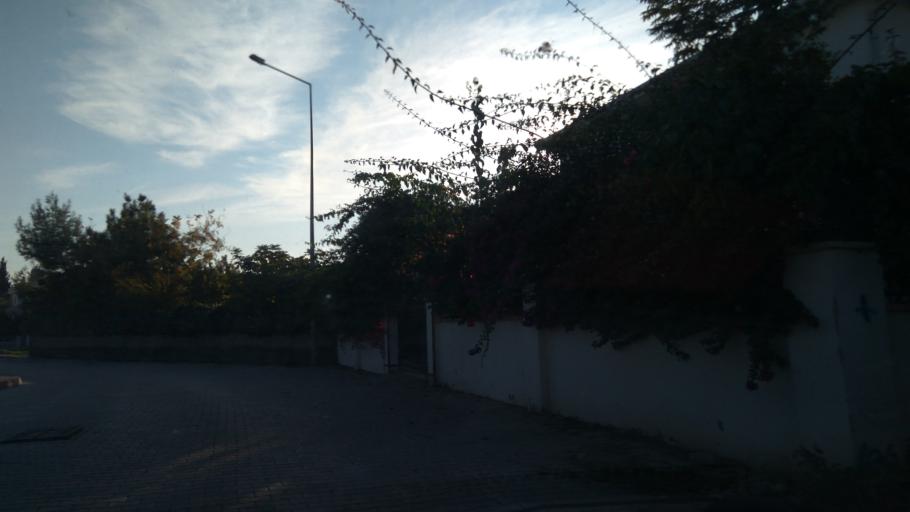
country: TR
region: Antalya
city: Kemer
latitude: 36.5662
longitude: 30.5601
